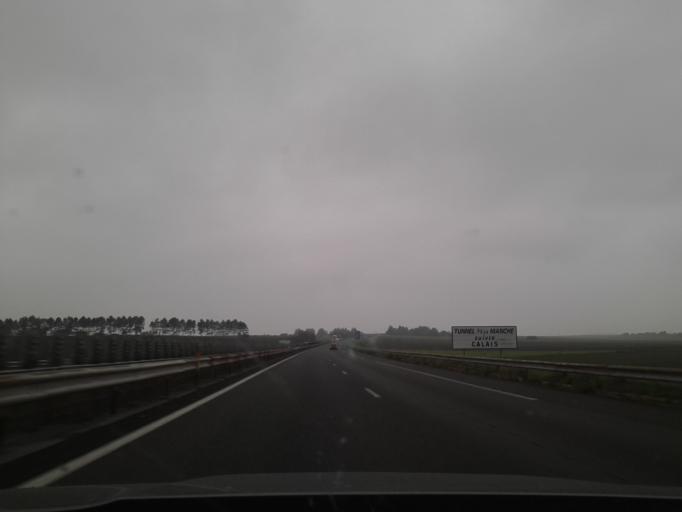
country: FR
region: Nord-Pas-de-Calais
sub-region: Departement du Nord
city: Fontaine-Notre-Dame
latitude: 50.1634
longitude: 3.1711
